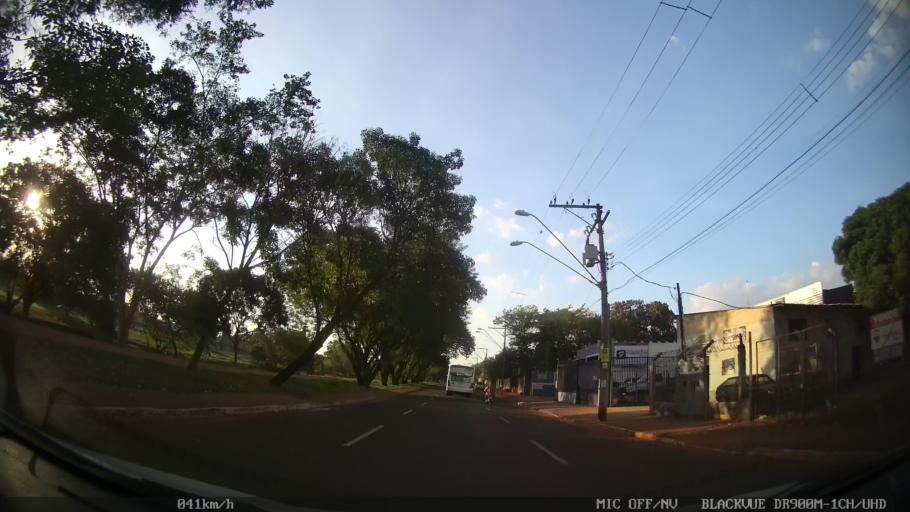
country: BR
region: Sao Paulo
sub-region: Ribeirao Preto
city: Ribeirao Preto
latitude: -21.1268
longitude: -47.8026
